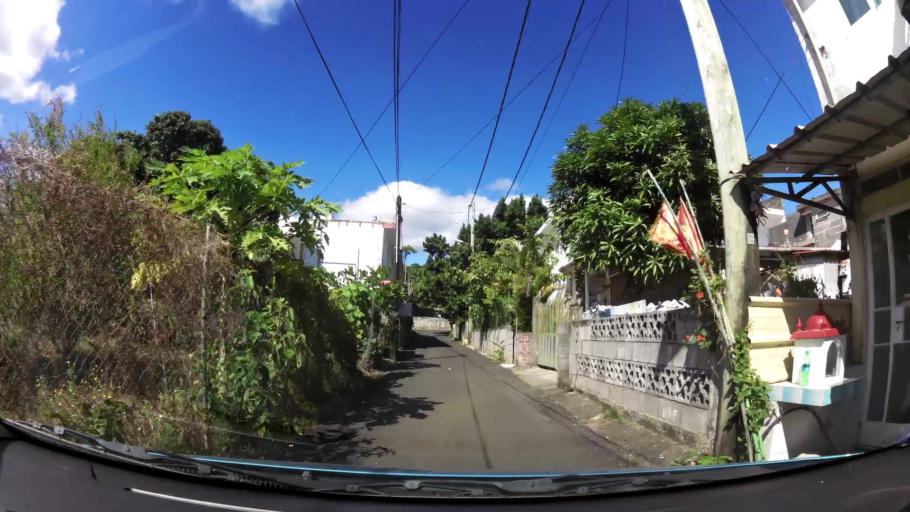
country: MU
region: Plaines Wilhems
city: Vacoas
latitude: -20.2895
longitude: 57.4759
